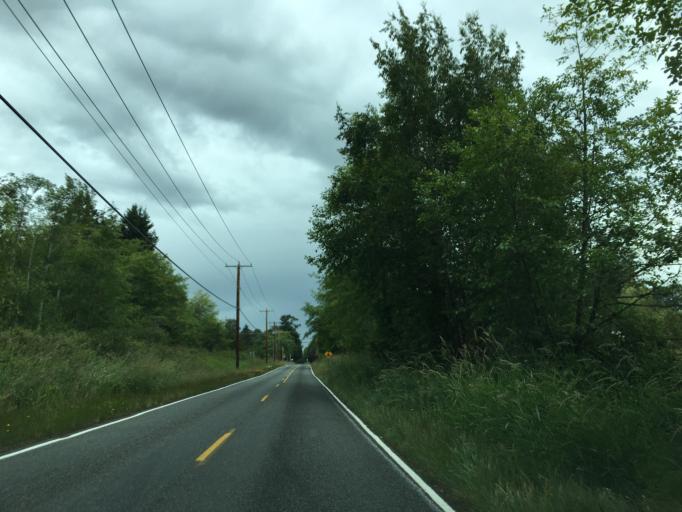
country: US
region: Washington
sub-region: Whatcom County
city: Birch Bay
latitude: 48.9433
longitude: -122.7507
